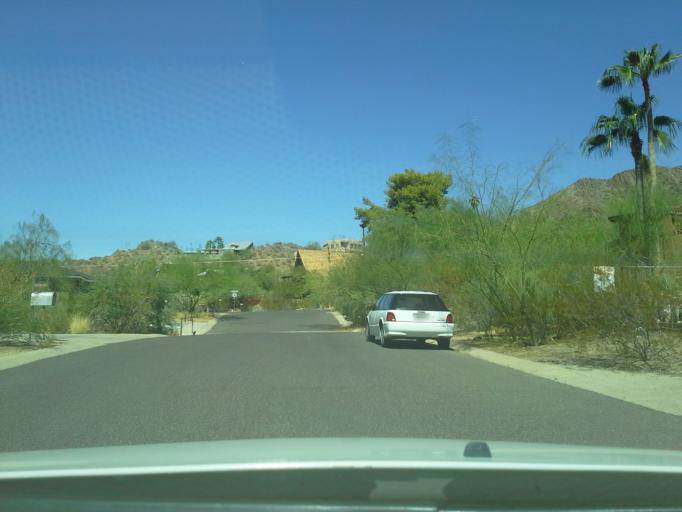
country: US
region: Arizona
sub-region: Maricopa County
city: Paradise Valley
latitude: 33.5759
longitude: -112.0468
